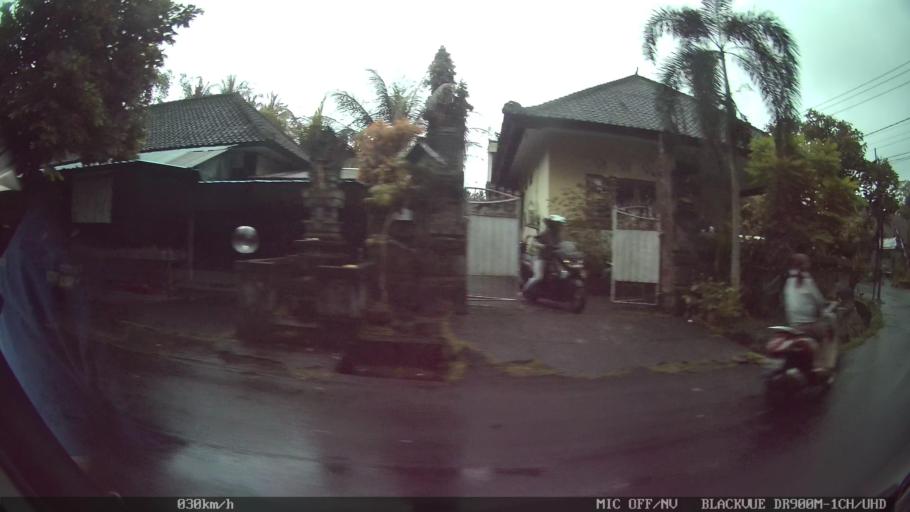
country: ID
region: Bali
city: Banjar Teguan
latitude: -8.5032
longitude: 115.2324
